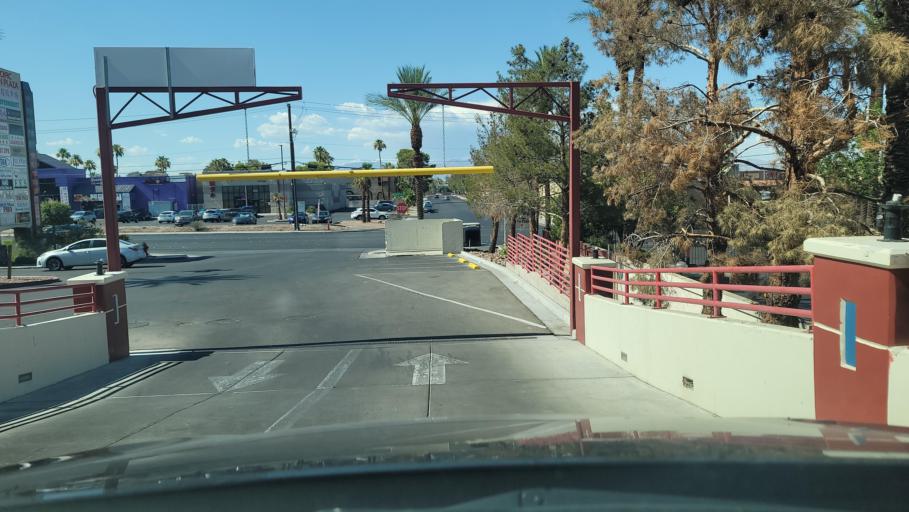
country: US
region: Nevada
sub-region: Clark County
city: Spring Valley
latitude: 36.1256
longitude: -115.2103
